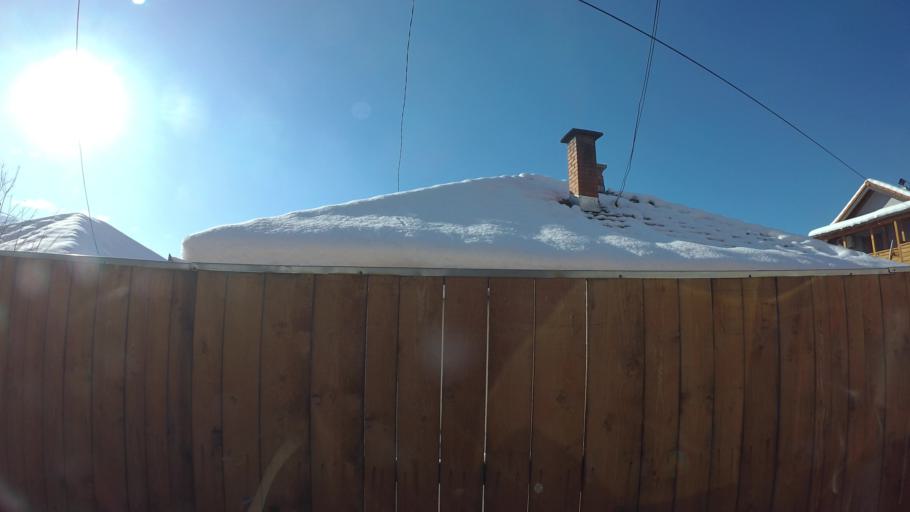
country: BA
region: Federation of Bosnia and Herzegovina
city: Kobilja Glava
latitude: 43.8736
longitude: 18.4241
